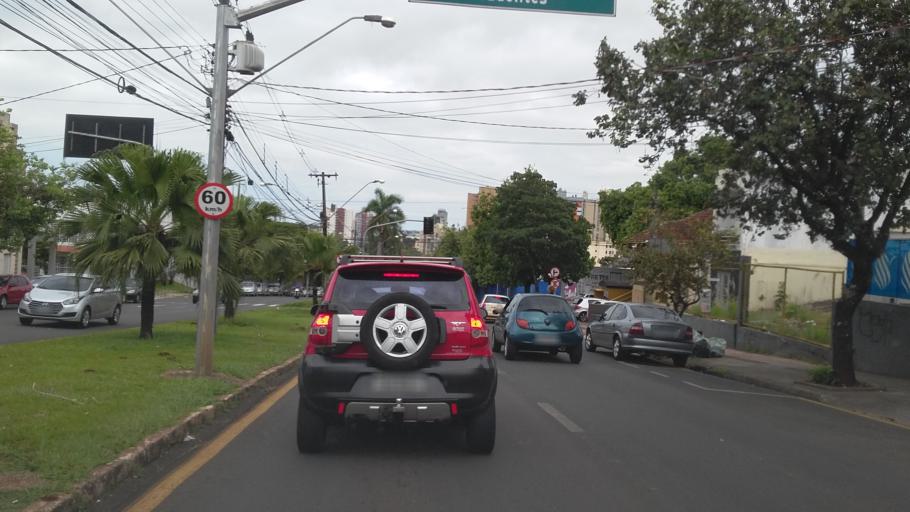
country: BR
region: Parana
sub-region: Londrina
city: Londrina
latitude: -23.3198
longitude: -51.1582
